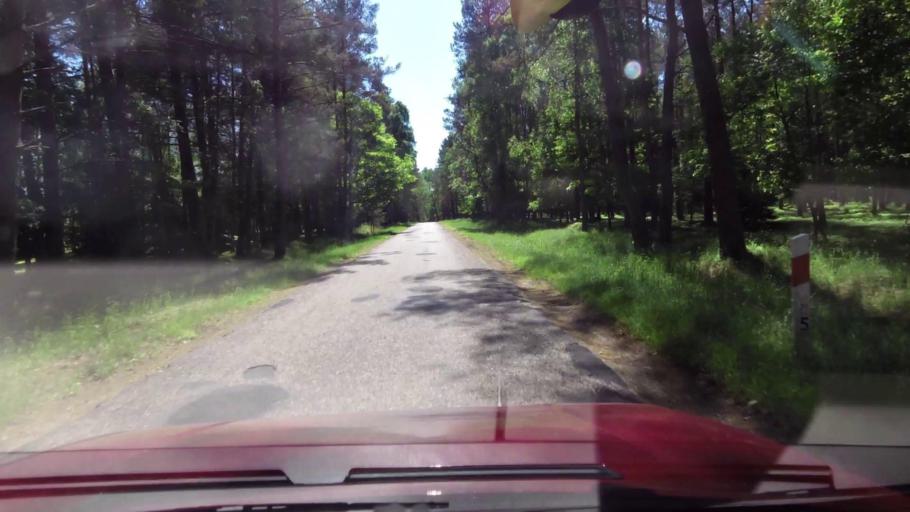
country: PL
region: West Pomeranian Voivodeship
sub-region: Powiat koszalinski
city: Bobolice
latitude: 54.0645
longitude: 16.5671
